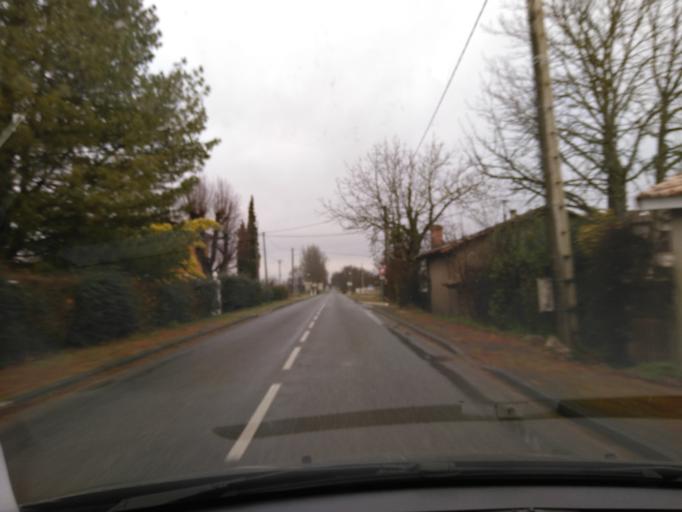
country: FR
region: Midi-Pyrenees
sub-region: Departement de la Haute-Garonne
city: Montesquieu-Volvestre
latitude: 43.1849
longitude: 1.2408
